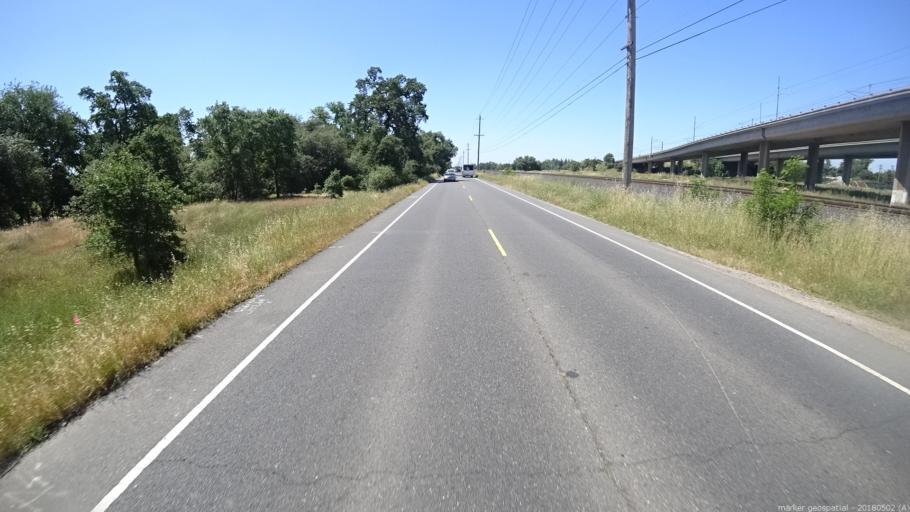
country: US
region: California
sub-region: Sacramento County
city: Arden-Arcade
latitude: 38.6343
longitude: -121.4096
